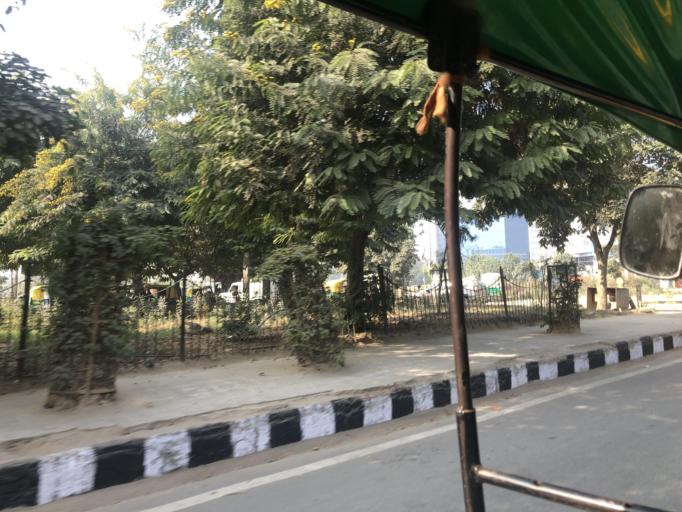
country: IN
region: Haryana
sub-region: Gurgaon
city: Gurgaon
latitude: 28.4525
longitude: 77.0753
